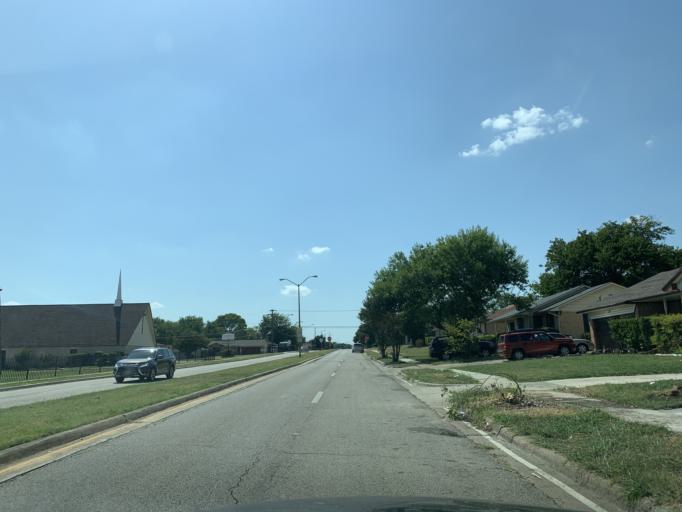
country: US
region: Texas
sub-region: Dallas County
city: Hutchins
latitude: 32.6750
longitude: -96.7996
